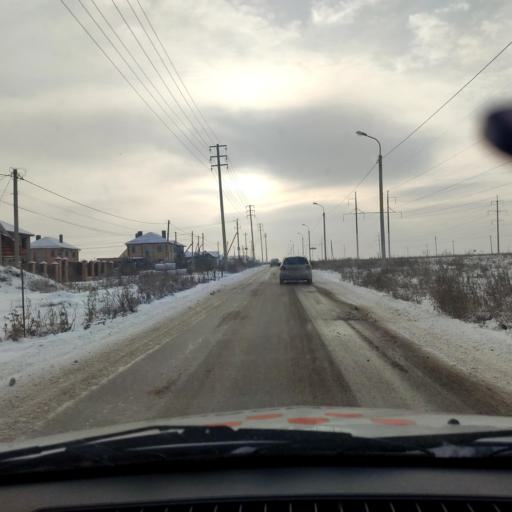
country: RU
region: Bashkortostan
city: Kabakovo
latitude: 54.6146
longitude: 56.0888
